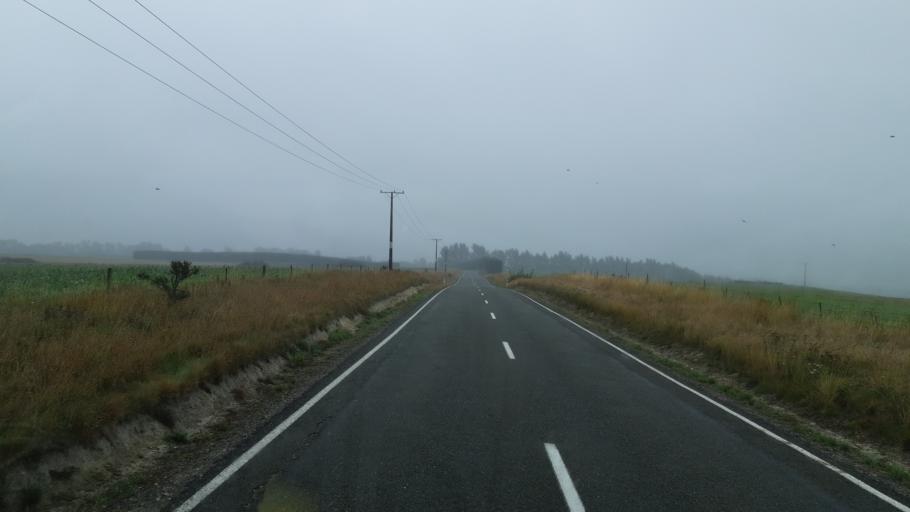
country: NZ
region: Otago
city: Oamaru
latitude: -44.9276
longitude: 170.8081
